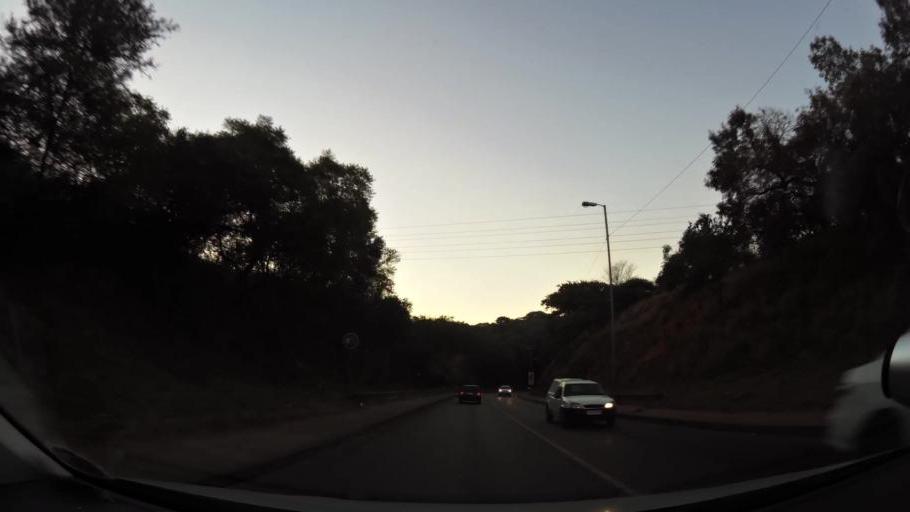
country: ZA
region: Gauteng
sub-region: City of Tshwane Metropolitan Municipality
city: Pretoria
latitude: -25.7352
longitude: 28.1361
